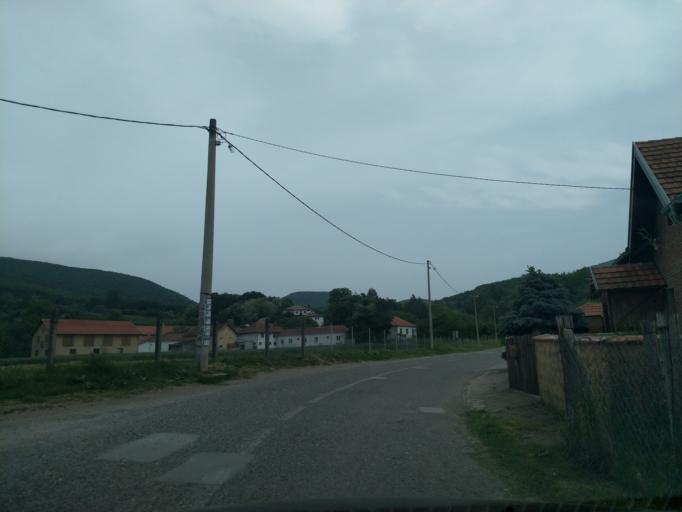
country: RS
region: Central Serbia
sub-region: Pomoravski Okrug
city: Paracin
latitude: 43.8571
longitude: 21.5955
